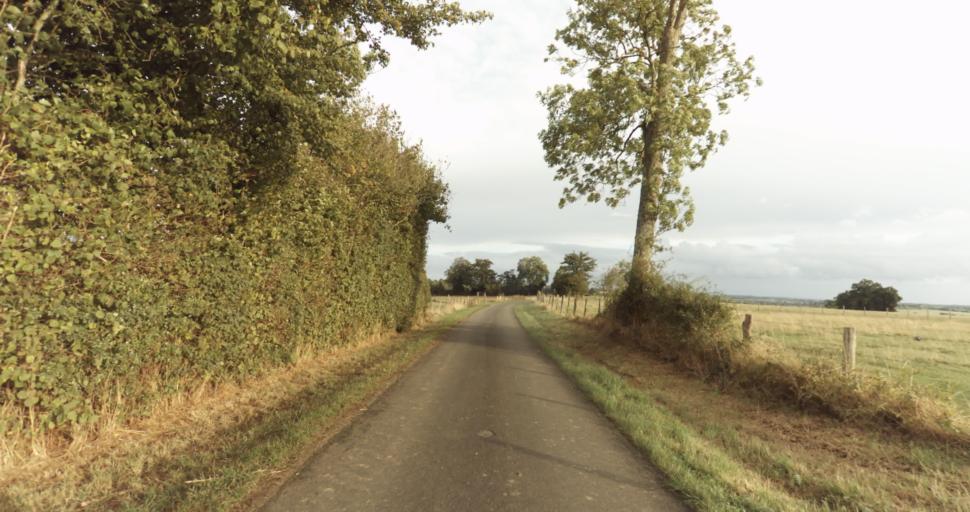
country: FR
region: Lower Normandy
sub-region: Departement de l'Orne
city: Sees
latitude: 48.6889
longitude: 0.2310
